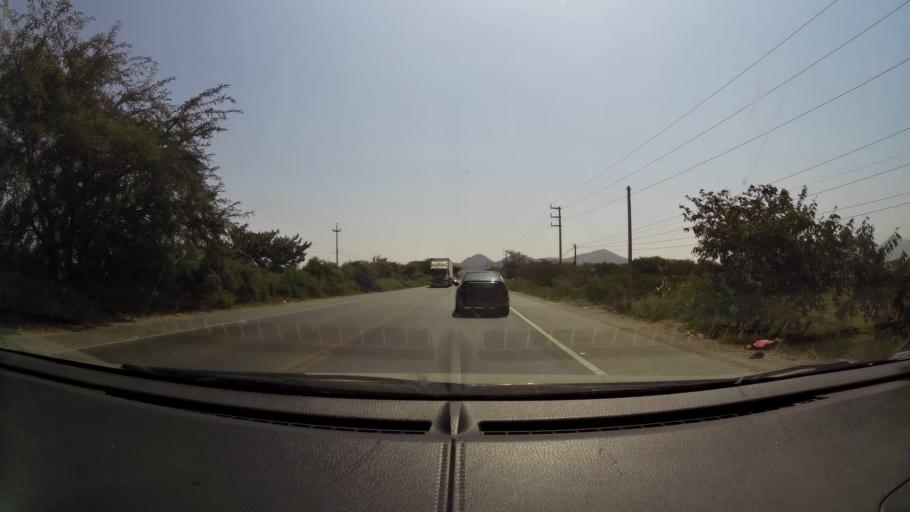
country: PE
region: Lambayeque
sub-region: Provincia de Chiclayo
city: Mocupe
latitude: -6.9844
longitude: -79.6331
